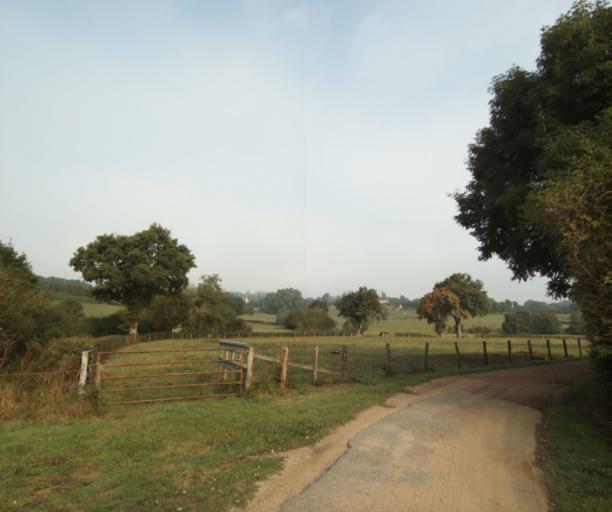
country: FR
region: Bourgogne
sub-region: Departement de Saone-et-Loire
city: Charolles
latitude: 46.4478
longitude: 4.2900
